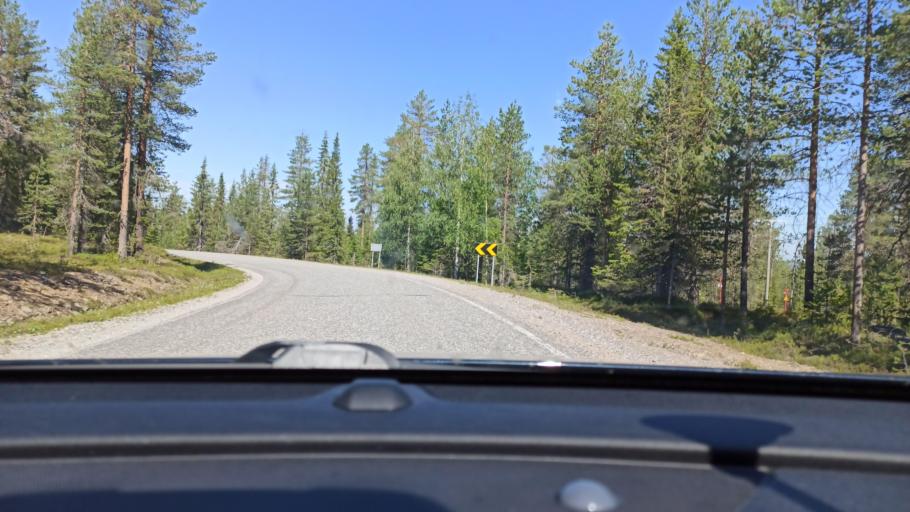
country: FI
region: Lapland
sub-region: Tunturi-Lappi
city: Kolari
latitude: 67.6820
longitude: 24.1366
